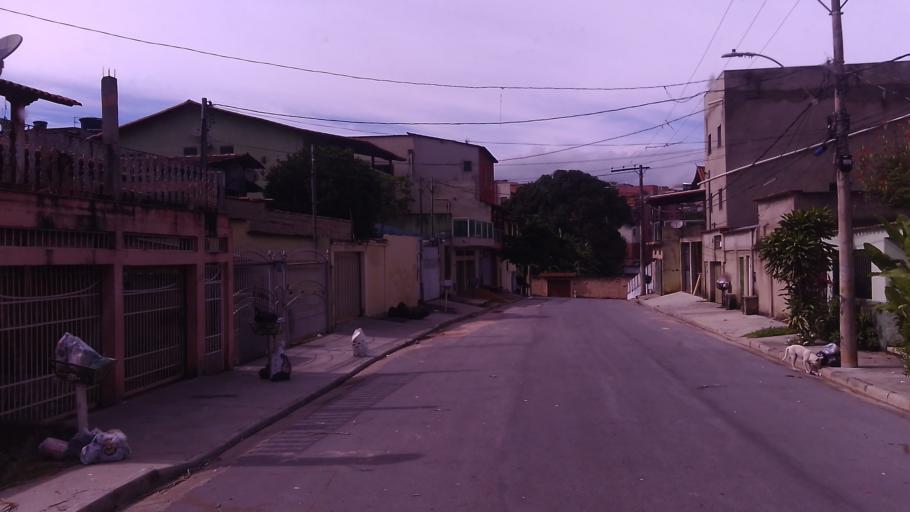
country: BR
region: Minas Gerais
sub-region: Santa Luzia
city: Santa Luzia
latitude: -19.8404
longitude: -43.8993
